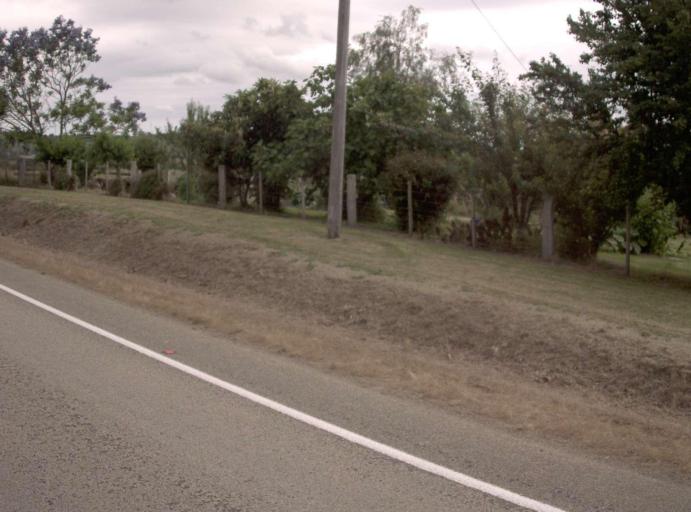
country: AU
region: Victoria
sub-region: East Gippsland
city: Lakes Entrance
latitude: -37.7169
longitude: 147.8393
